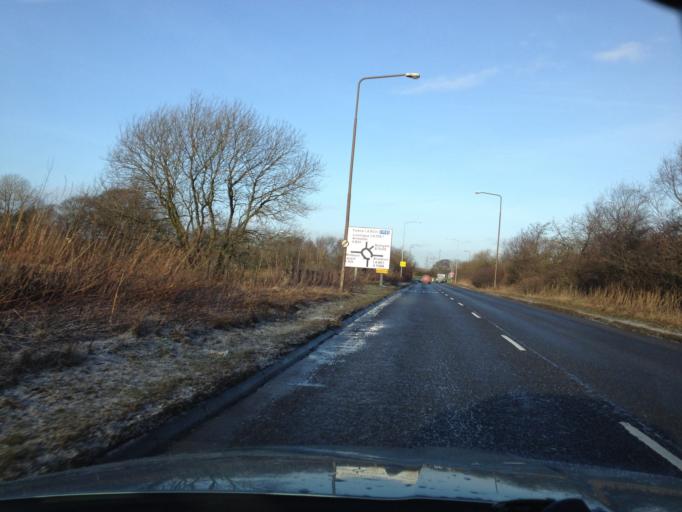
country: GB
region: Scotland
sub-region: West Lothian
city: Blackburn
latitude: 55.8785
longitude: -3.6580
